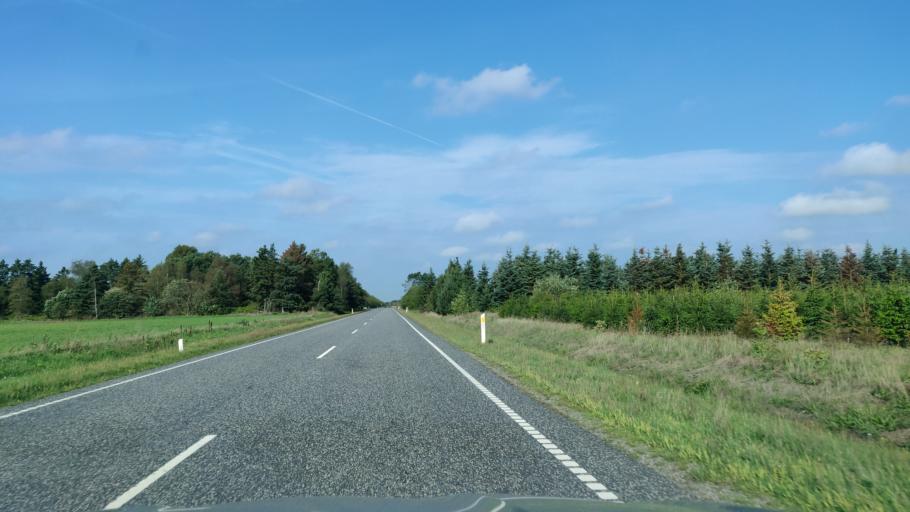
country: DK
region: Central Jutland
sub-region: Herning Kommune
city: Sunds
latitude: 56.2448
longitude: 9.0781
